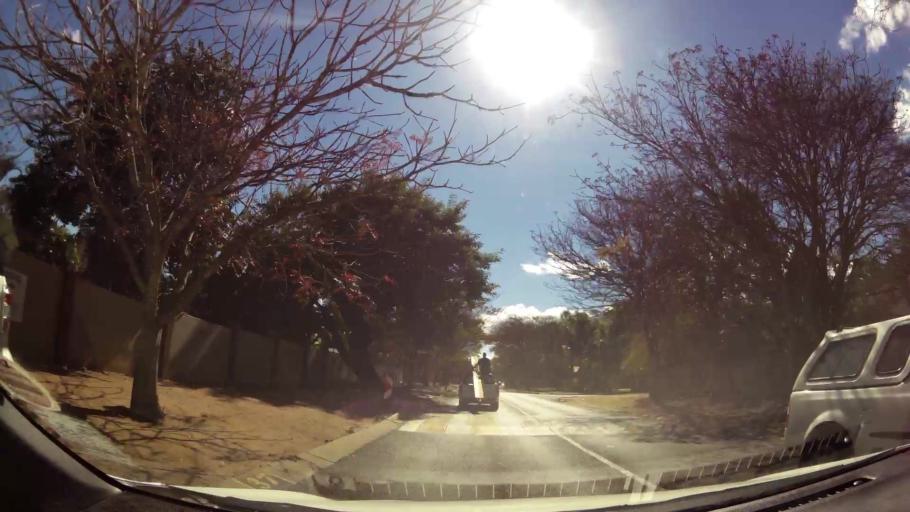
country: ZA
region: Limpopo
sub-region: Capricorn District Municipality
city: Polokwane
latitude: -23.9085
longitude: 29.4785
